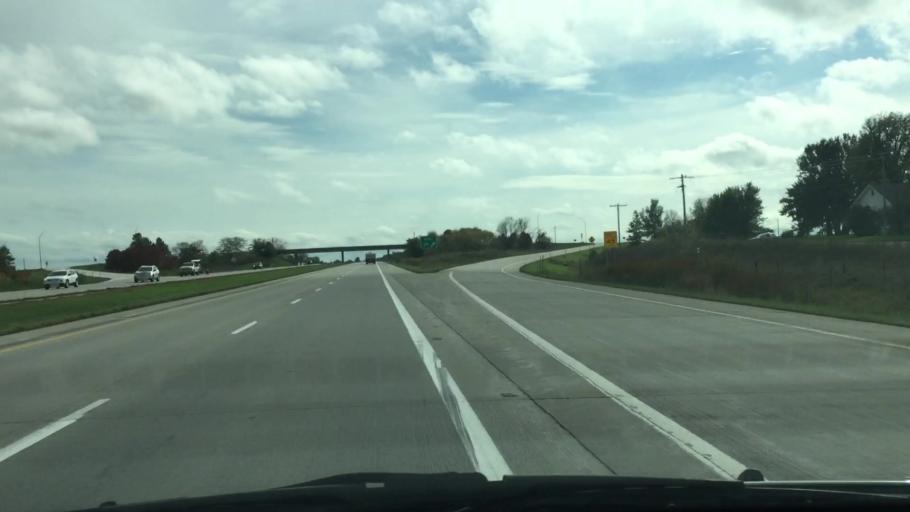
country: US
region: Iowa
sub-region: Clarke County
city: Osceola
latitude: 40.9757
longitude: -93.7977
